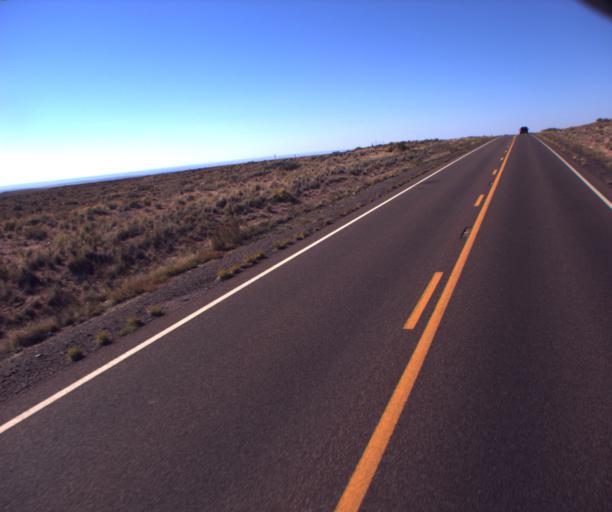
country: US
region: Arizona
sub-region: Navajo County
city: Joseph City
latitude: 35.1605
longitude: -110.4589
